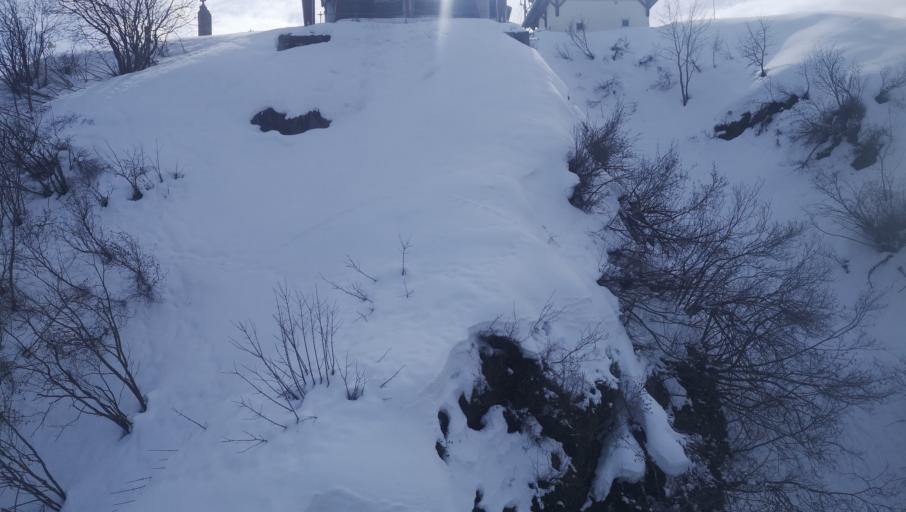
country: FR
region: Rhone-Alpes
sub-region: Departement de la Haute-Savoie
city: Megeve
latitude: 45.8339
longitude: 6.6133
